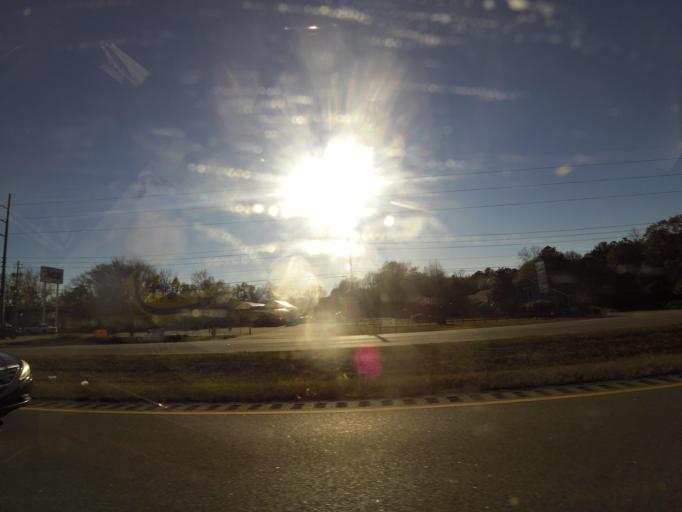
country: US
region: Alabama
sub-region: Houston County
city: Dothan
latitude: 31.2014
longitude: -85.4174
